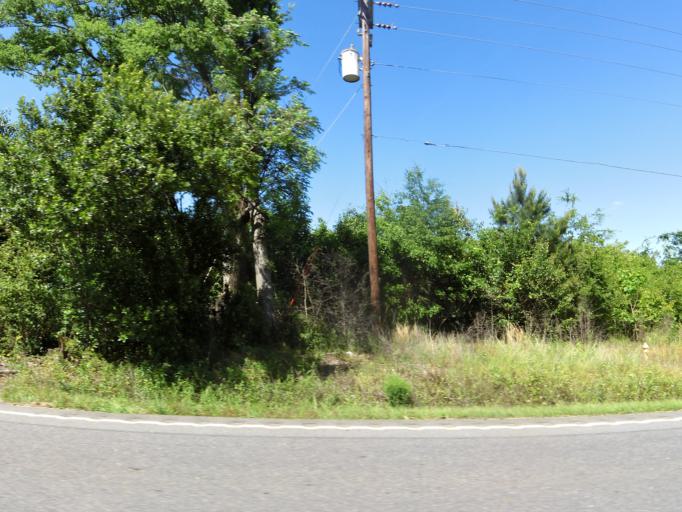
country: US
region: South Carolina
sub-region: Aiken County
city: Aiken
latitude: 33.5323
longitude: -81.6433
